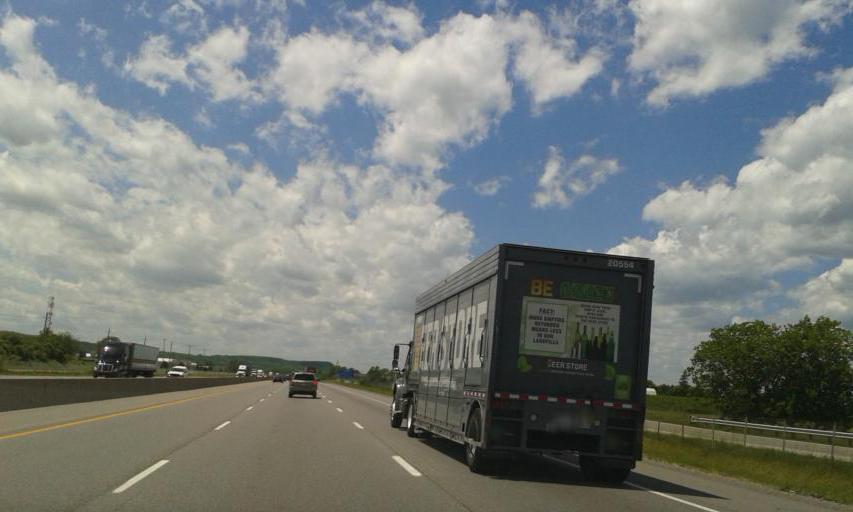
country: CA
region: Ontario
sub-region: Regional Municipality of Niagara
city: St. Catharines
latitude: 43.1894
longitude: -79.5014
